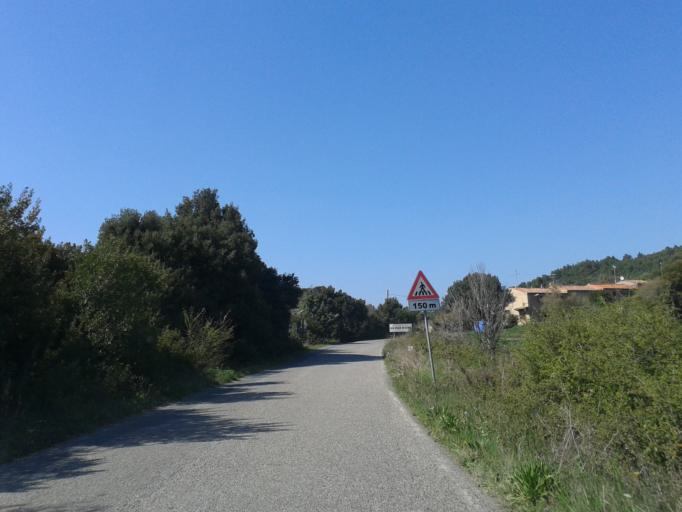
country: IT
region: Tuscany
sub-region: Provincia di Livorno
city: Quercianella
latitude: 43.4536
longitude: 10.4030
